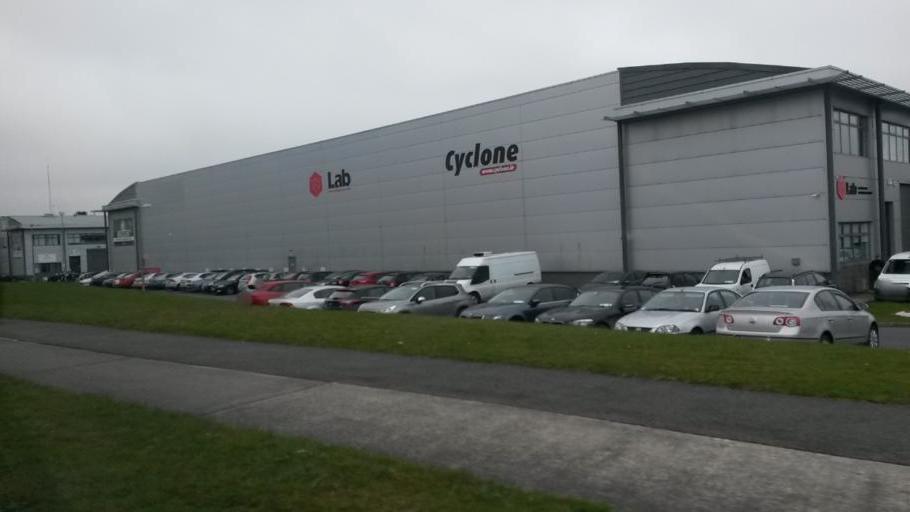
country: IE
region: Leinster
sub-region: Dublin City
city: Finglas
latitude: 53.4009
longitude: -6.3168
